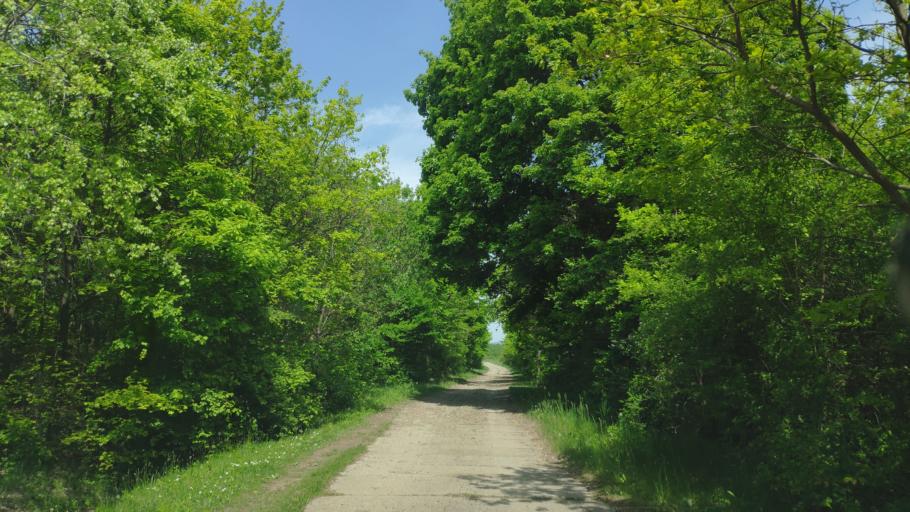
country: SK
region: Kosicky
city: Secovce
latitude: 48.6957
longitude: 21.5967
